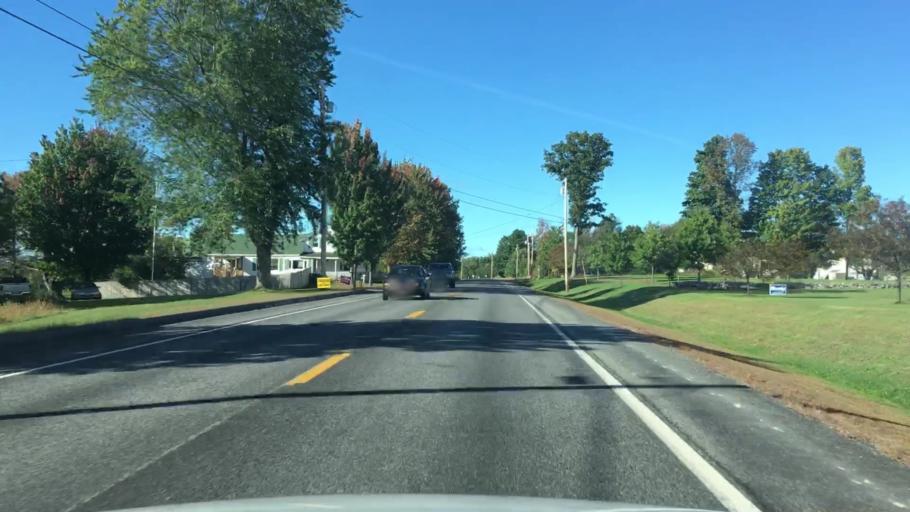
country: US
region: Maine
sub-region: Androscoggin County
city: Lisbon Falls
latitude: 44.0274
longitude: -70.0674
